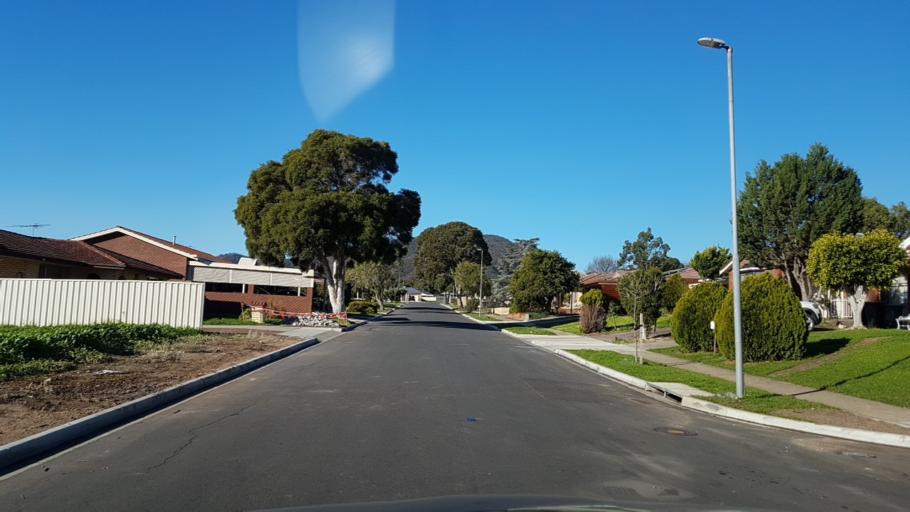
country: AU
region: South Australia
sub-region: Campbelltown
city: Campbelltown
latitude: -34.8834
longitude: 138.6838
